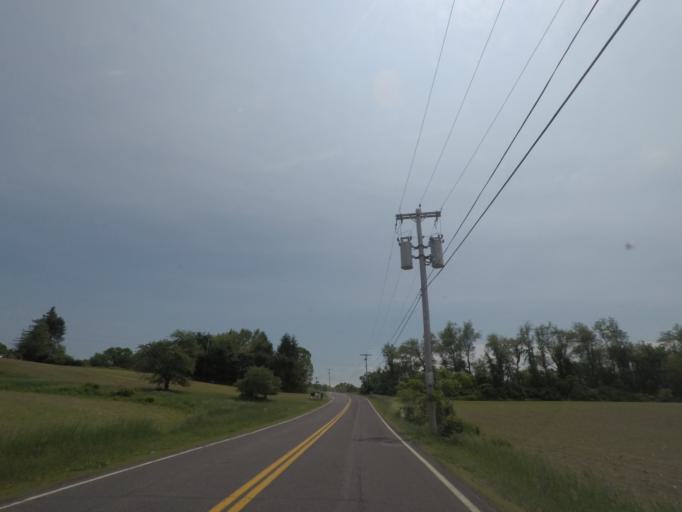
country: US
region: New York
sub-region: Columbia County
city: Niverville
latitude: 42.4725
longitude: -73.6909
